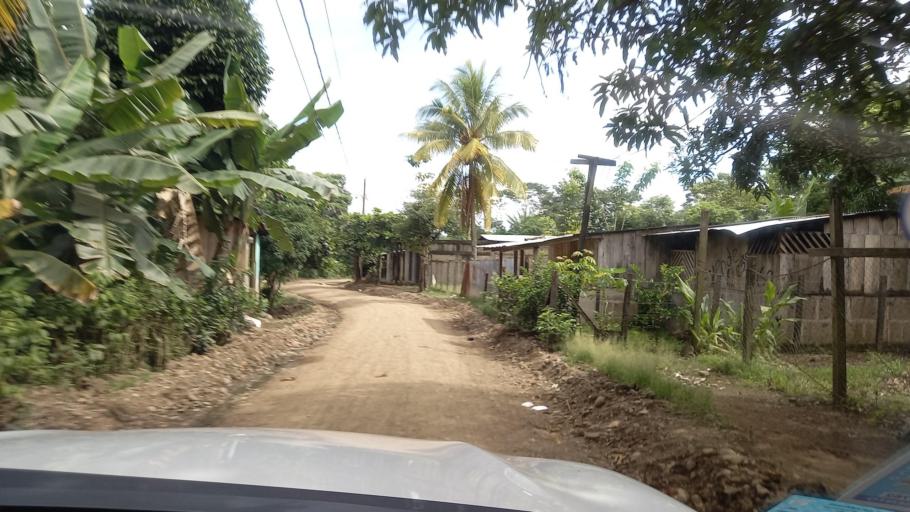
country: NI
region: Jinotega
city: San Jose de Bocay
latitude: 13.3729
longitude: -85.6840
